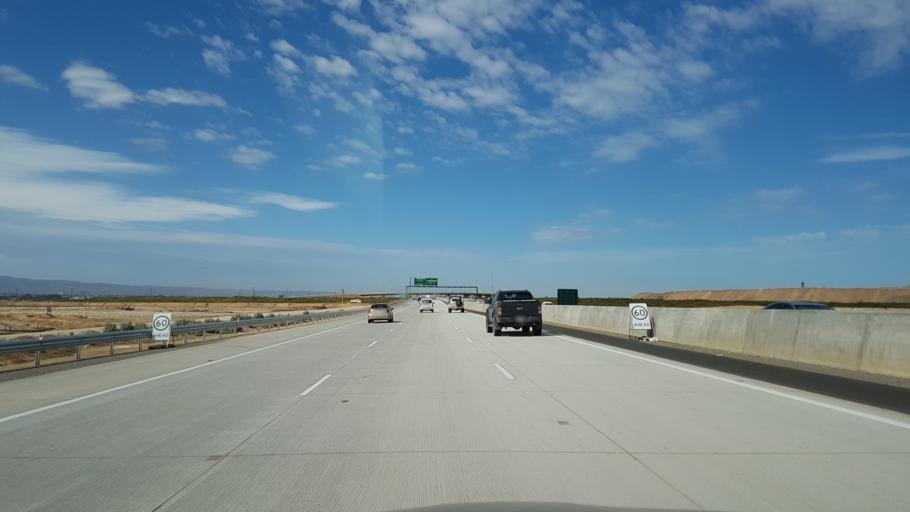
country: AU
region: South Australia
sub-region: Port Adelaide Enfield
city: Enfield
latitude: -34.8199
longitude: 138.5620
